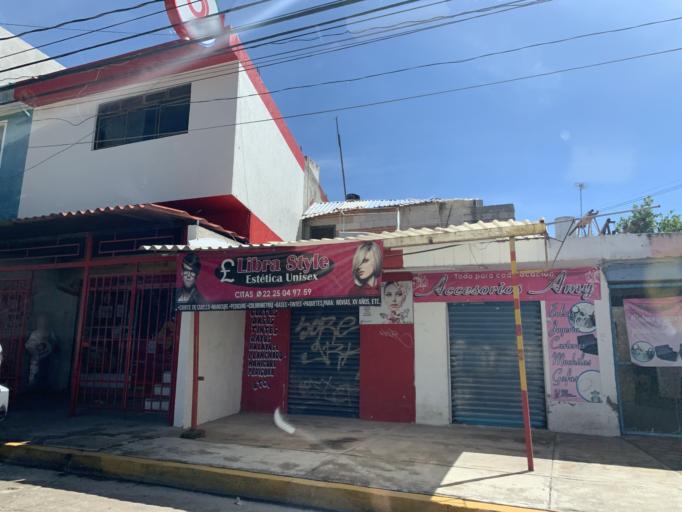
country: MX
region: Puebla
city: Cuautlancingo
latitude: 19.0971
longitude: -98.2713
